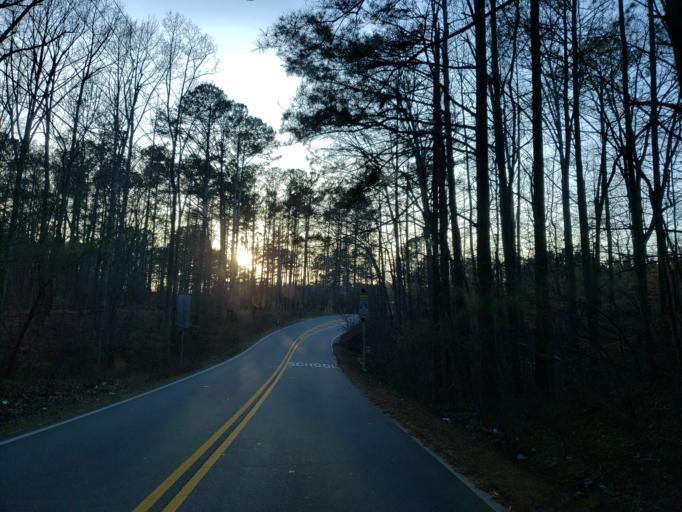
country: US
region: Georgia
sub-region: Cobb County
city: Acworth
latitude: 34.0257
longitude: -84.7332
